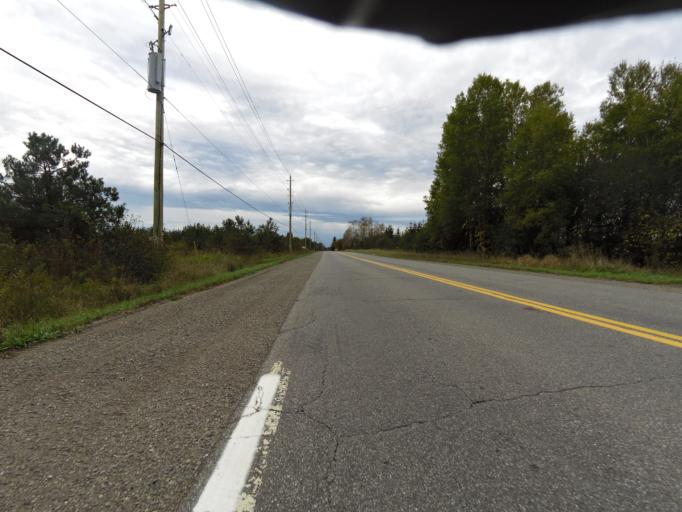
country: CA
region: Ontario
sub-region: Lanark County
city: Smiths Falls
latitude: 44.9568
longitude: -75.8232
